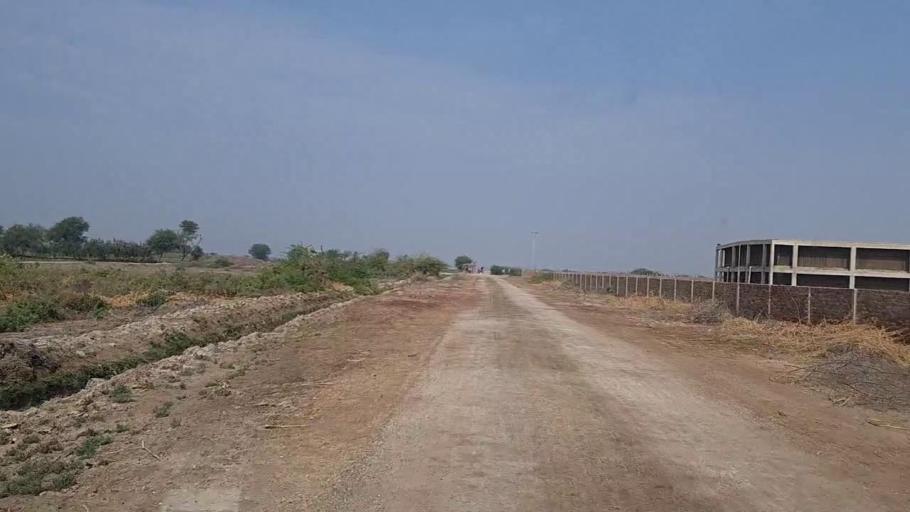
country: PK
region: Sindh
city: Mirwah Gorchani
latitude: 25.3486
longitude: 69.0637
